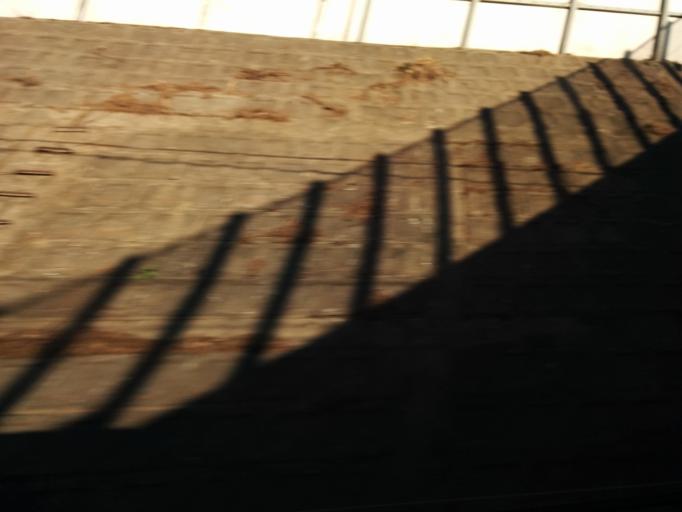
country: JP
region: Kanagawa
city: Minami-rinkan
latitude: 35.4305
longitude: 139.4611
